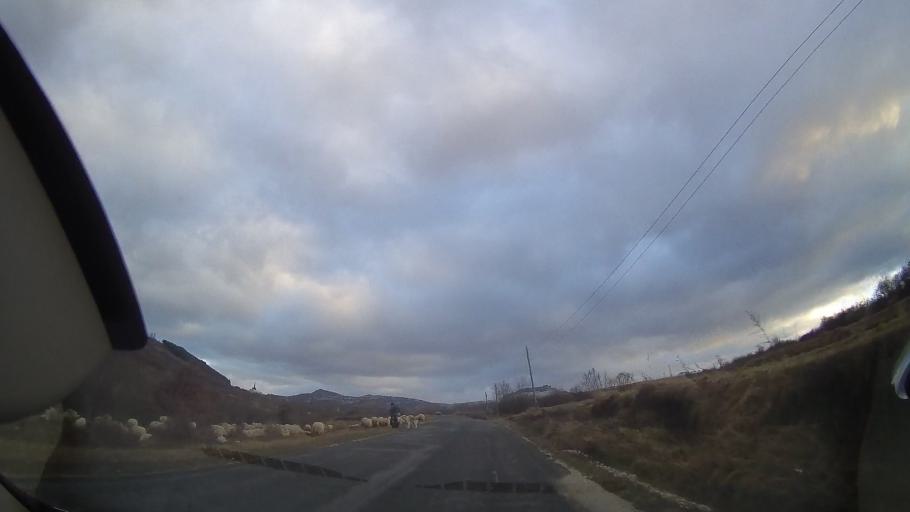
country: RO
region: Cluj
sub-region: Comuna Calatele
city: Calatele
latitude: 46.7854
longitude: 23.0154
